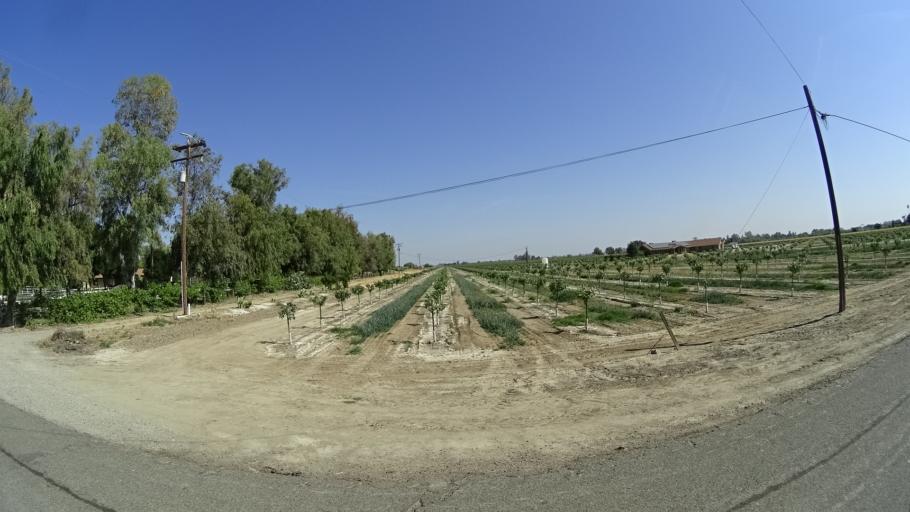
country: US
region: California
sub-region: Fresno County
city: Riverdale
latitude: 36.3513
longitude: -119.8649
